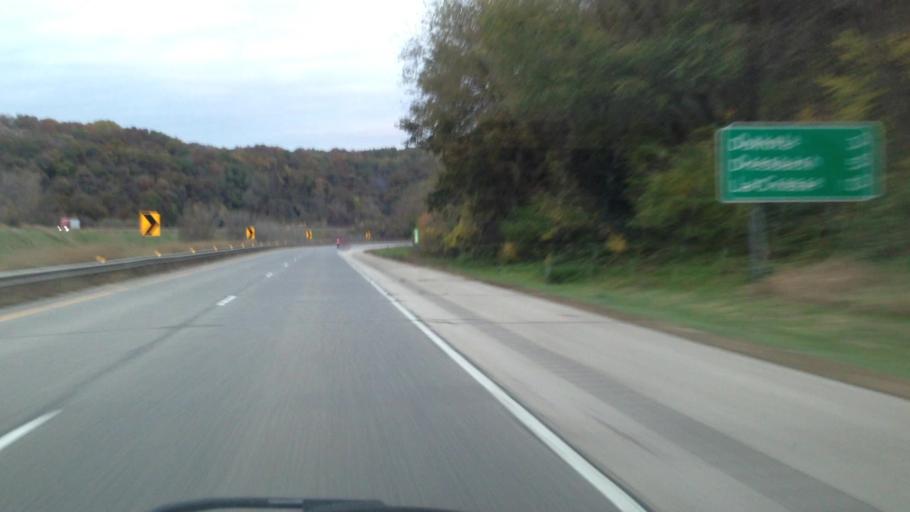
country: US
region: Wisconsin
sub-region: Trempealeau County
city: Trempealeau
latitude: 43.9317
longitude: -91.4242
